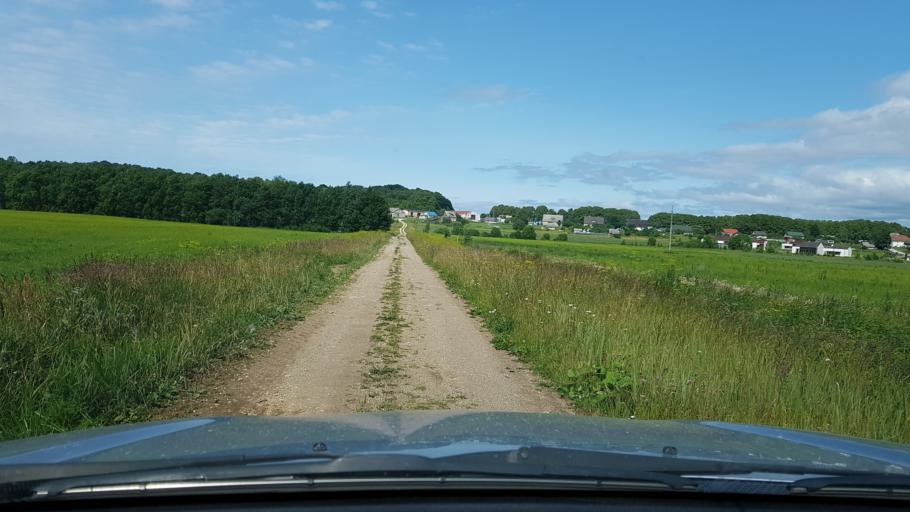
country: EE
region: Ida-Virumaa
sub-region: Sillamaee linn
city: Sillamae
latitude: 59.3677
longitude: 27.8672
